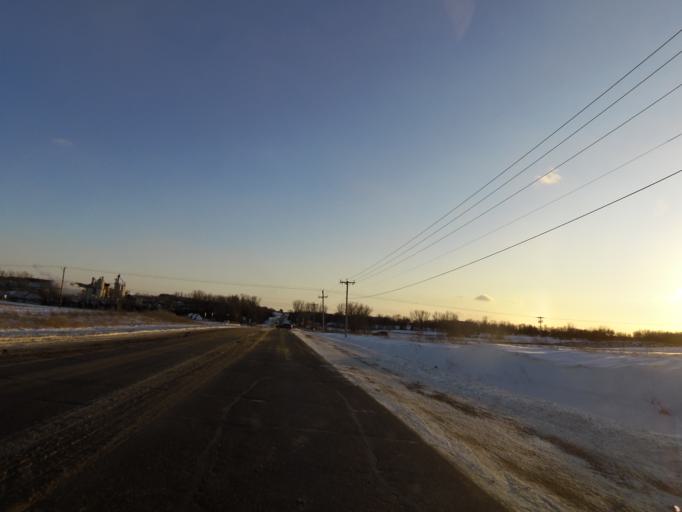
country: US
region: Minnesota
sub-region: Washington County
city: Lake Elmo
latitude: 44.9465
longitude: -92.8832
